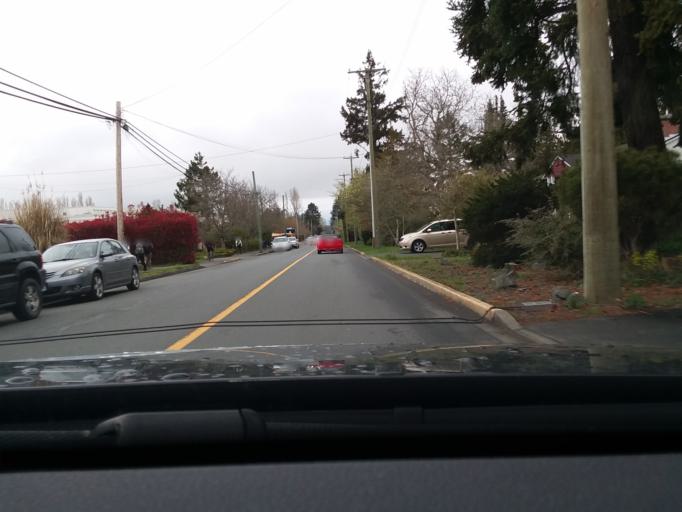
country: CA
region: British Columbia
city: Victoria
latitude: 48.5148
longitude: -123.3741
